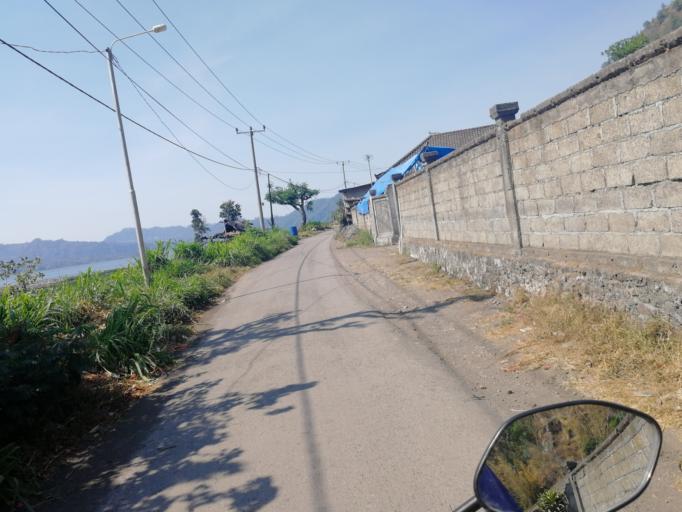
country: ID
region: Bali
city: Banjar Trunyan
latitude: -8.2664
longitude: 115.4198
